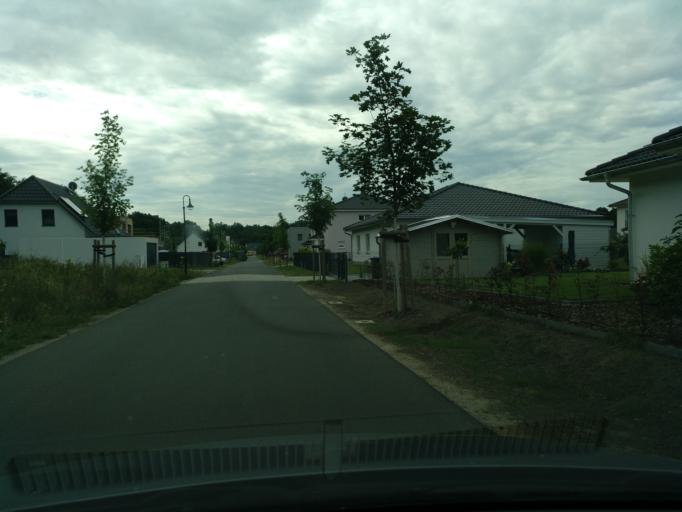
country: DE
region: Brandenburg
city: Bad Saarow
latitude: 52.2777
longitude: 14.0675
